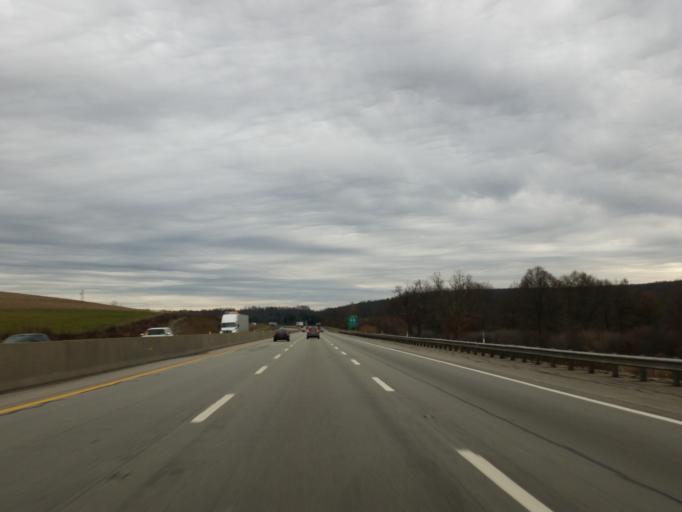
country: US
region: Pennsylvania
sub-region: Fayette County
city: Bear Rocks
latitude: 40.1355
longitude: -79.4094
